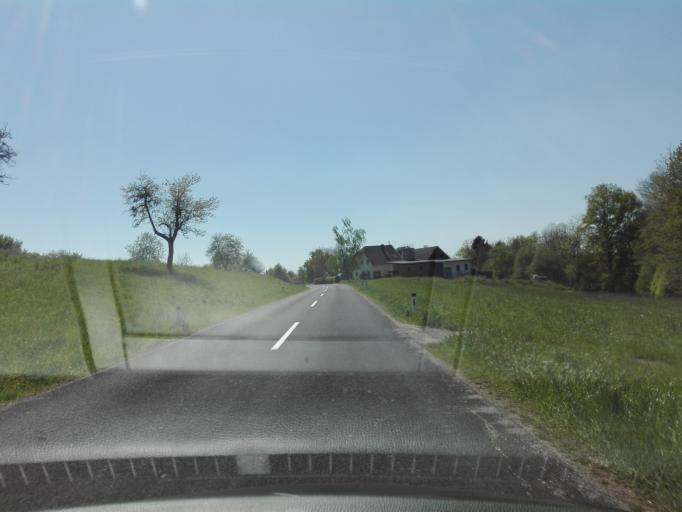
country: AT
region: Upper Austria
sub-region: Politischer Bezirk Rohrbach
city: Kleinzell im Muehlkreis
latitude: 48.3598
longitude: 13.9155
